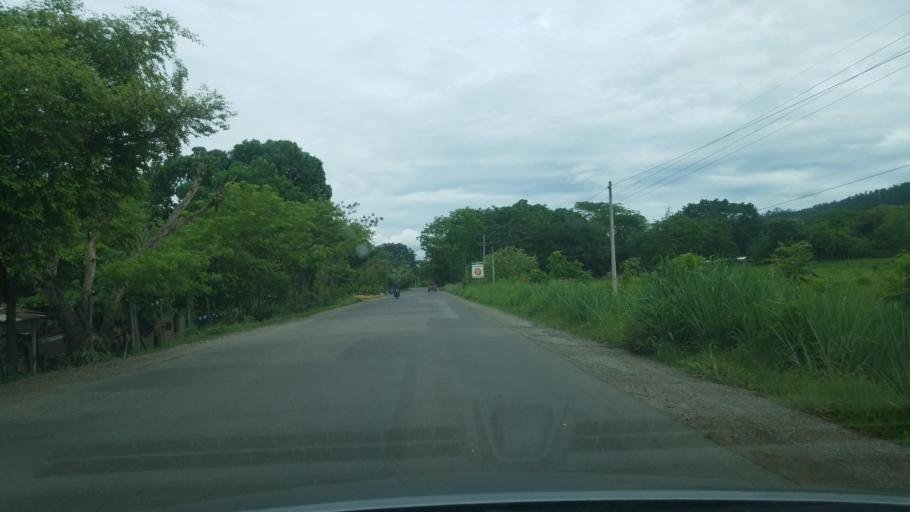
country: HN
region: Santa Barbara
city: La Flecha
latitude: 15.2980
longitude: -88.4706
